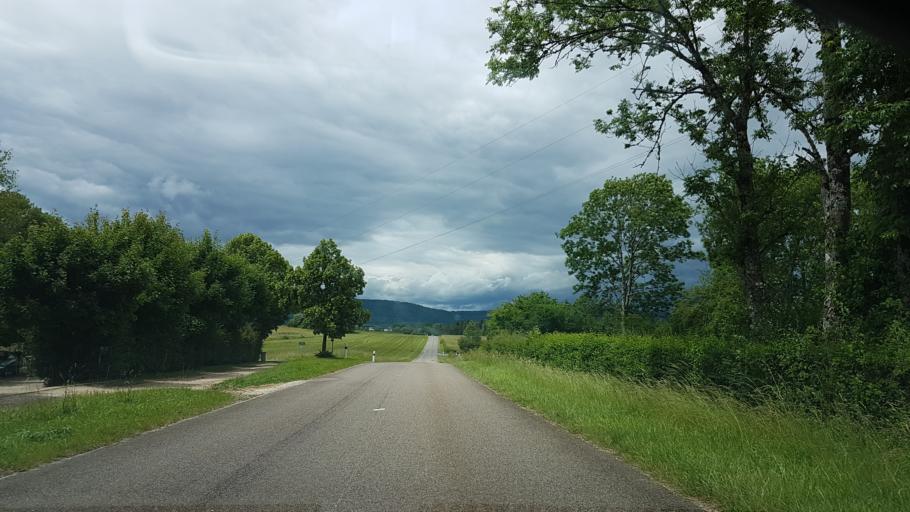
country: FR
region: Franche-Comte
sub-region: Departement du Jura
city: Clairvaux-les-Lacs
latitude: 46.5809
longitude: 5.7292
